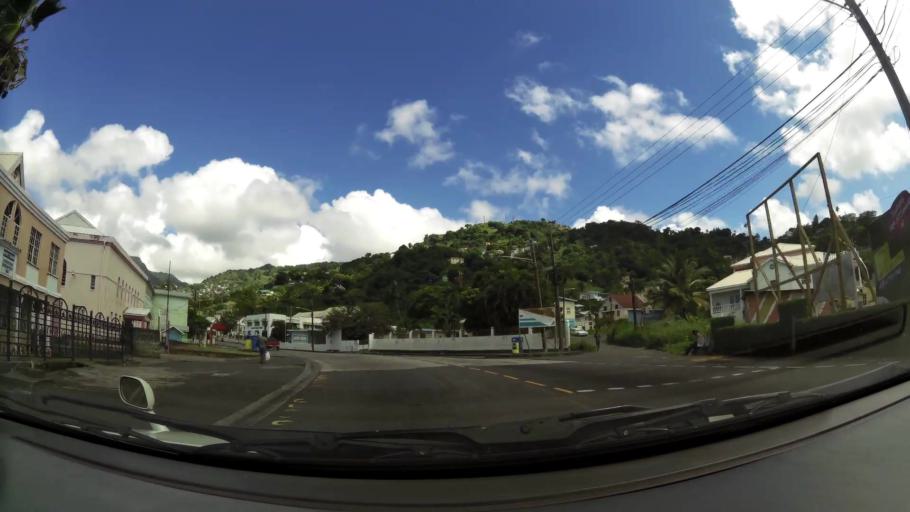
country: VC
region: Saint George
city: Kingstown
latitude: 13.1530
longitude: -61.2218
